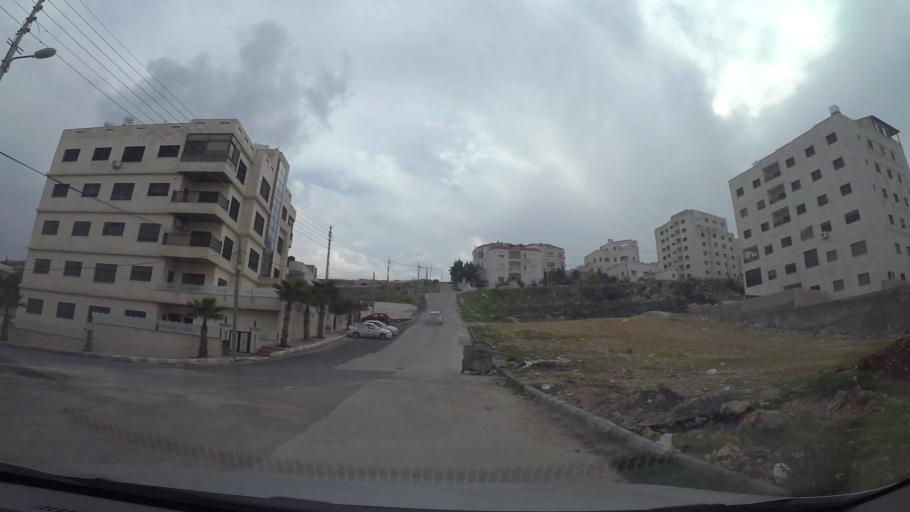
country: JO
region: Amman
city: Umm as Summaq
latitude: 31.8825
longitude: 35.8653
